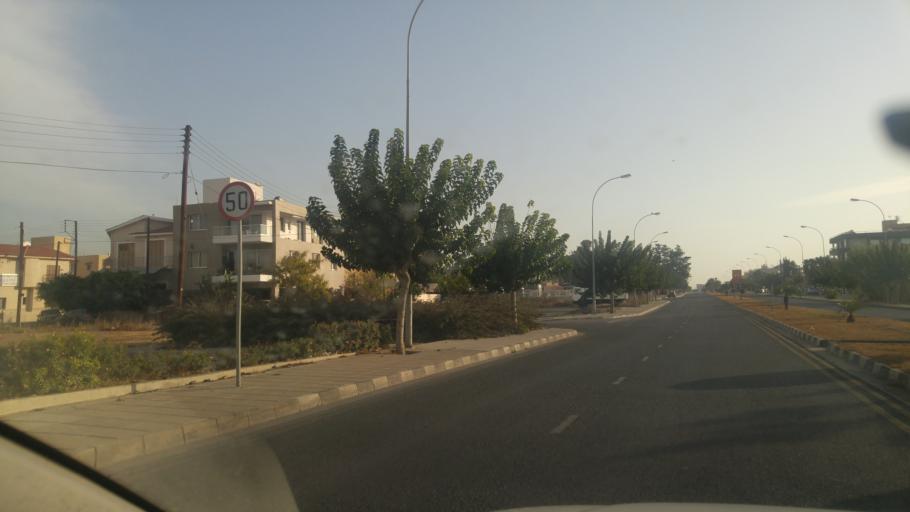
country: CY
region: Limassol
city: Pano Polemidia
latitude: 34.6773
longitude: 33.0000
